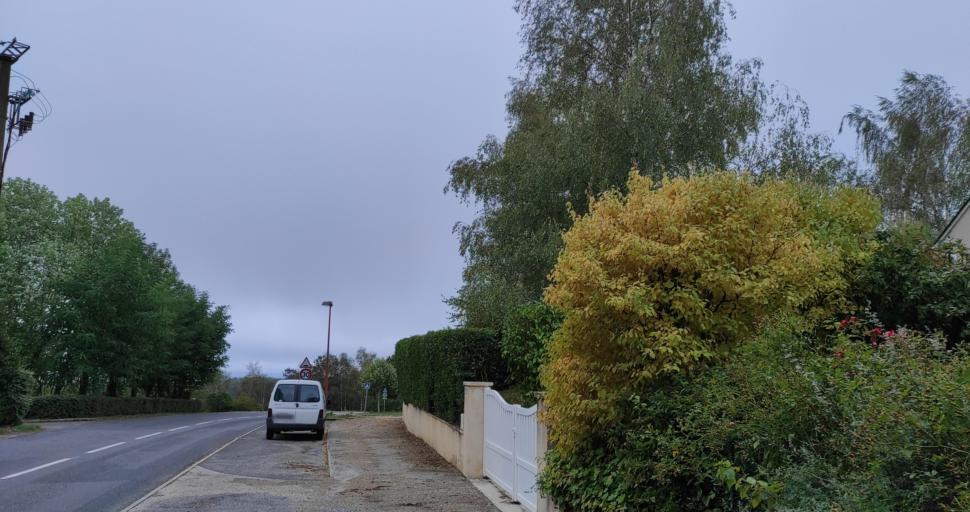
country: FR
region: Midi-Pyrenees
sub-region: Departement de l'Aveyron
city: Baraqueville
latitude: 44.2737
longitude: 2.4356
